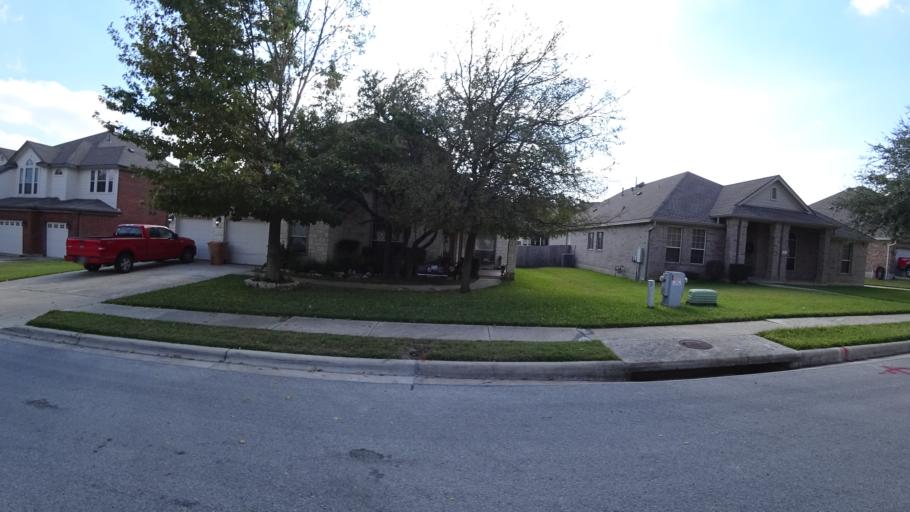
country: US
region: Texas
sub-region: Travis County
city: Shady Hollow
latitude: 30.1621
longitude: -97.8490
